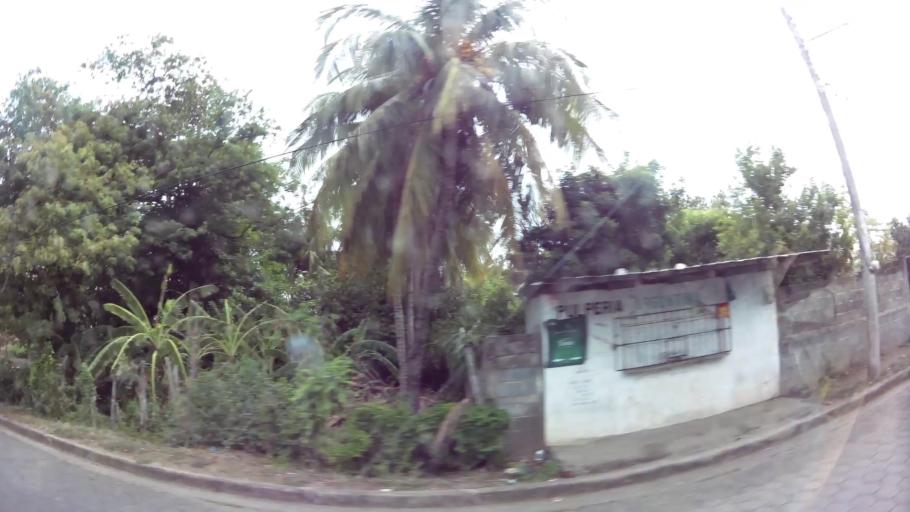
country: NI
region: Rivas
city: Rivas
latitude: 11.4354
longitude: -85.8317
